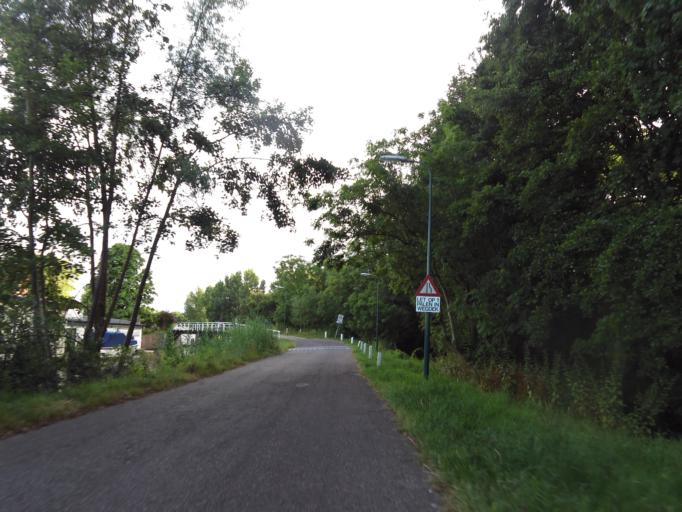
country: NL
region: South Holland
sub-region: Gemeente Oegstgeest
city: Oegstgeest
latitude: 52.1800
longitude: 4.4874
